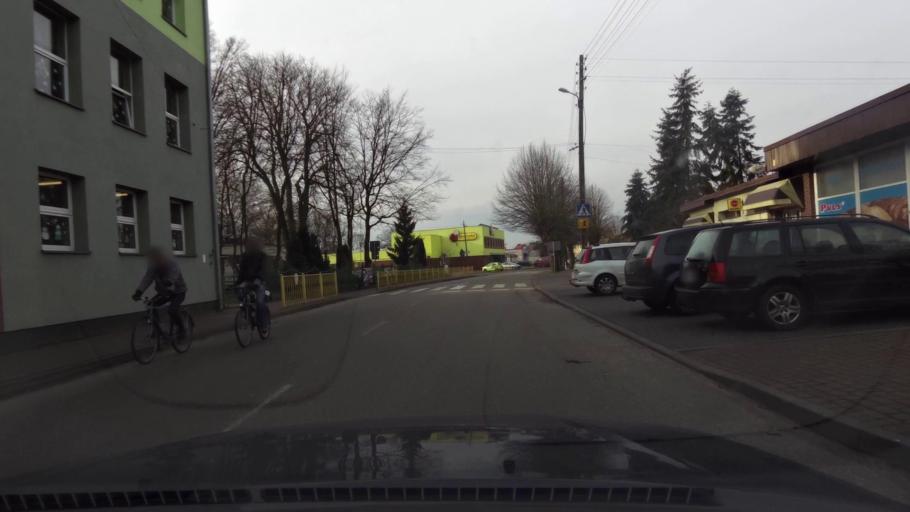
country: PL
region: West Pomeranian Voivodeship
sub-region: Powiat goleniowski
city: Stepnica
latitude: 53.6519
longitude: 14.6263
